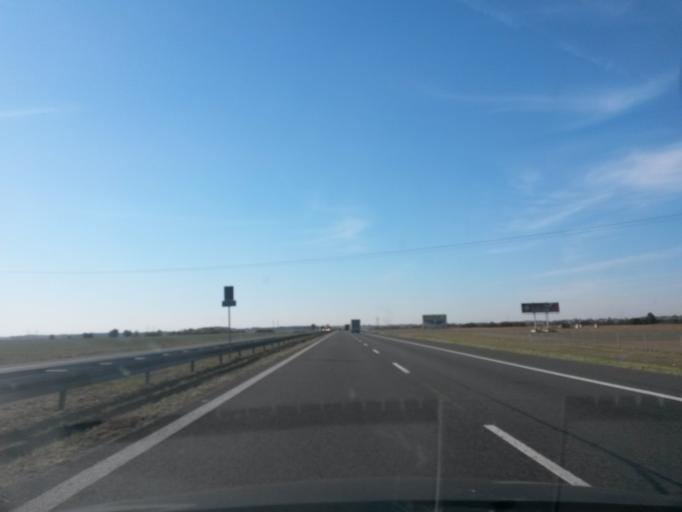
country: PL
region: Opole Voivodeship
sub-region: Powiat brzeski
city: Lewin Brzeski
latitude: 50.7115
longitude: 17.5889
